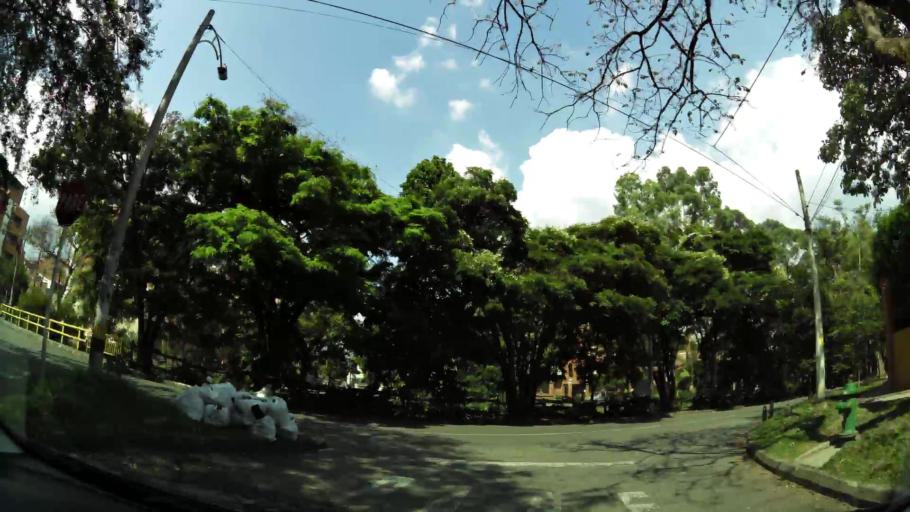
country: CO
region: Antioquia
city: Itagui
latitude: 6.2167
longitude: -75.5953
